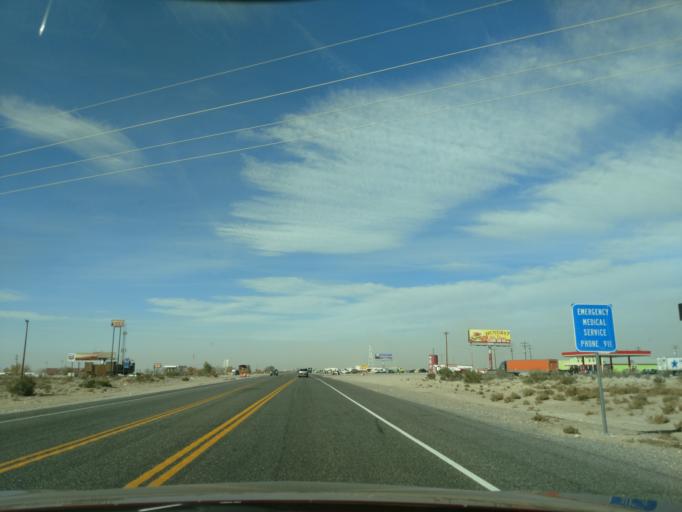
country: US
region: Nevada
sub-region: Nye County
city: Beatty
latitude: 36.6423
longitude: -116.3943
